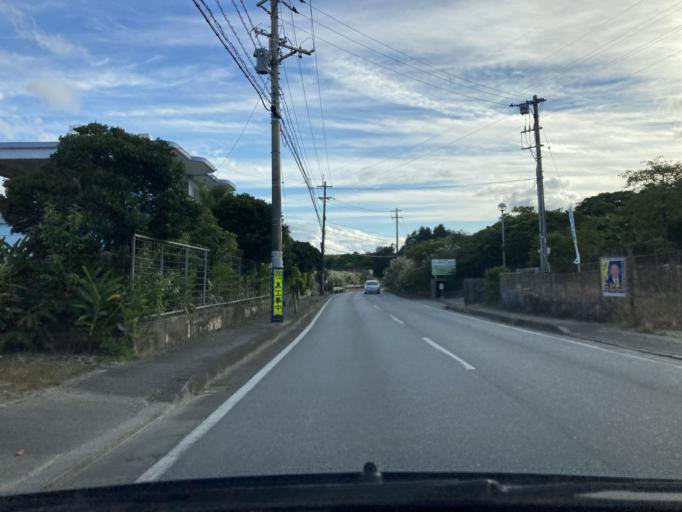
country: JP
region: Okinawa
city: Tomigusuku
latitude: 26.1618
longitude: 127.7389
